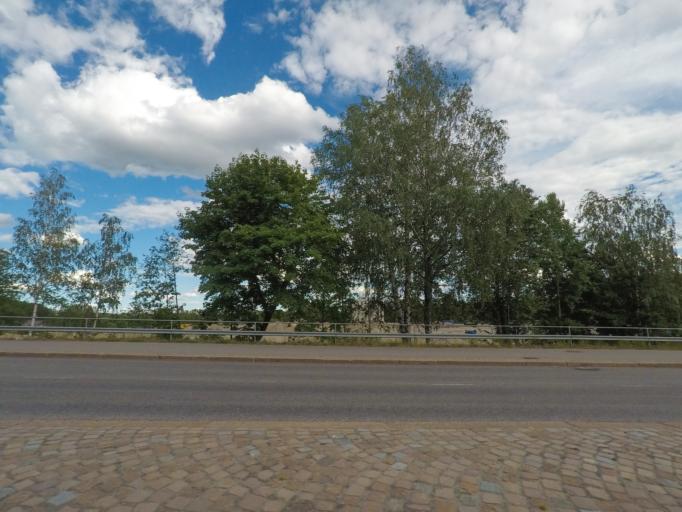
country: FI
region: Paijanne Tavastia
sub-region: Lahti
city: Lahti
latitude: 60.9758
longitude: 25.6385
